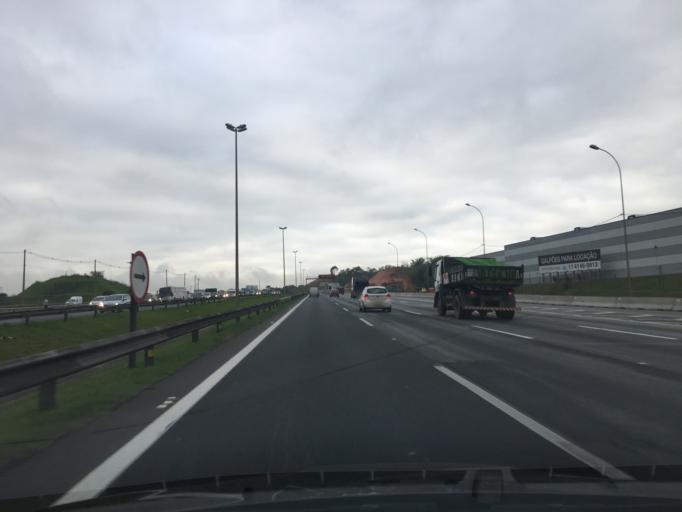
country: BR
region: Sao Paulo
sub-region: Osasco
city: Osasco
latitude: -23.5590
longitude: -46.8198
